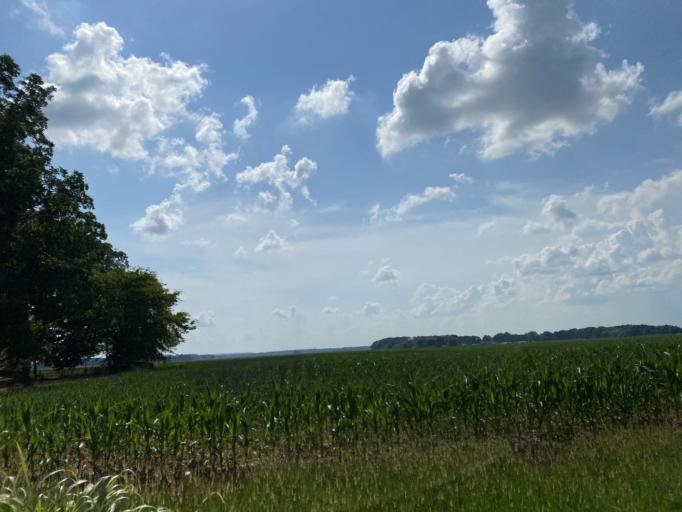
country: US
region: Alabama
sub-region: Lawrence County
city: Town Creek
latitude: 34.6716
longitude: -87.4060
